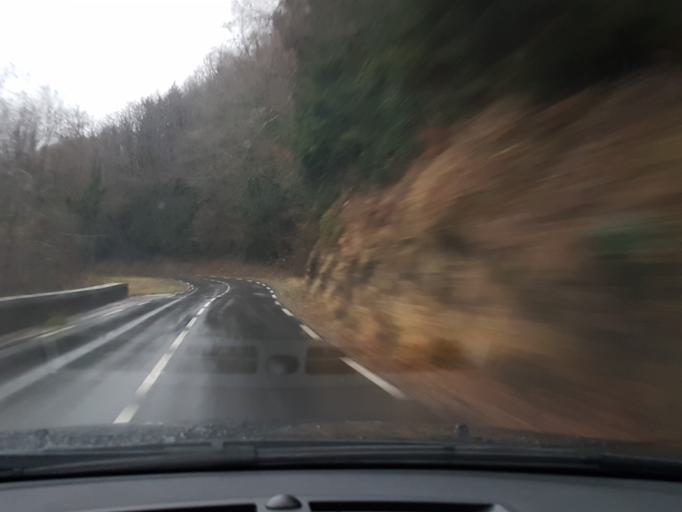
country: FR
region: Midi-Pyrenees
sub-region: Departement de l'Ariege
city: Saint-Girons
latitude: 42.9334
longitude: 1.1775
